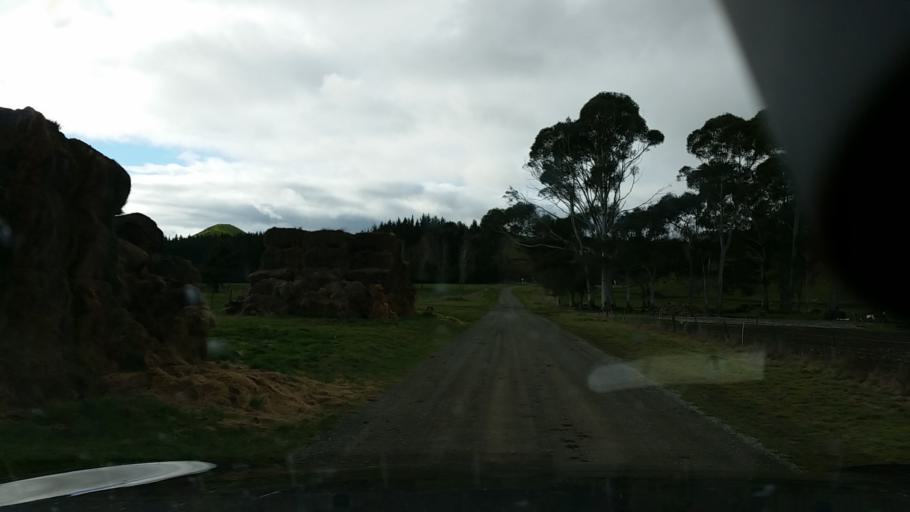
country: NZ
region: Marlborough
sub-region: Marlborough District
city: Blenheim
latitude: -41.6589
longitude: 173.6595
